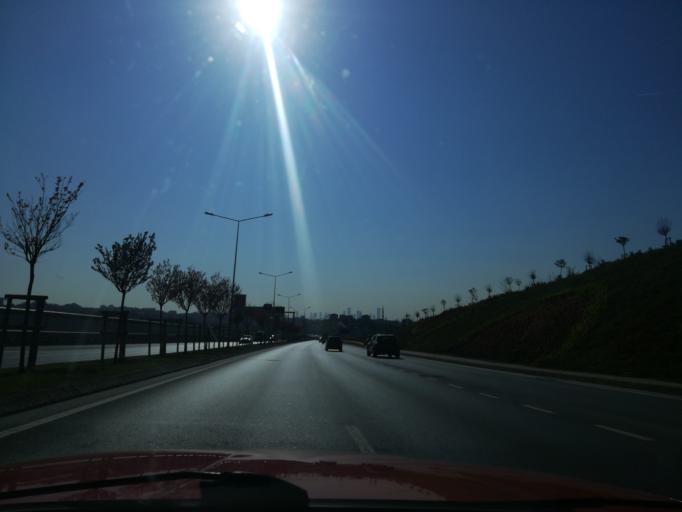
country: TR
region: Istanbul
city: Umraniye
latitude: 41.1068
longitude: 29.1071
